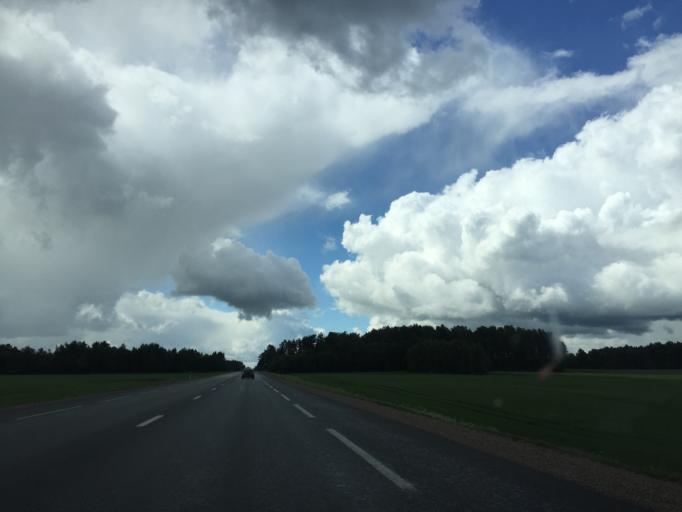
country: LV
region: Lecava
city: Iecava
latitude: 56.6577
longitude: 24.2313
